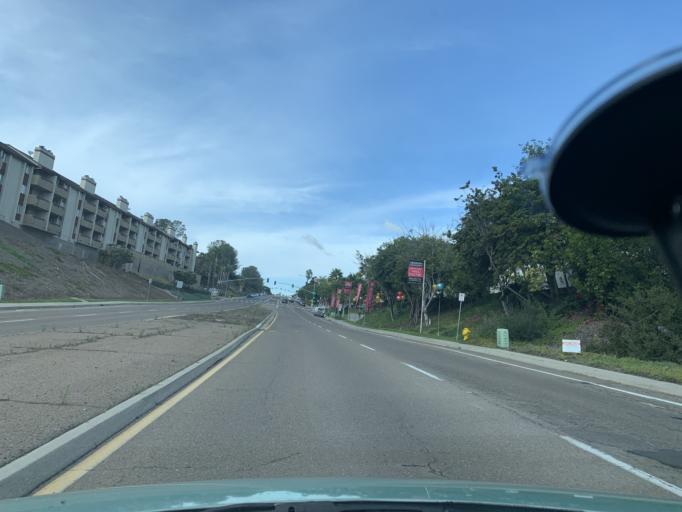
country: US
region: California
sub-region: San Diego County
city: San Diego
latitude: 32.8129
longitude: -117.1786
